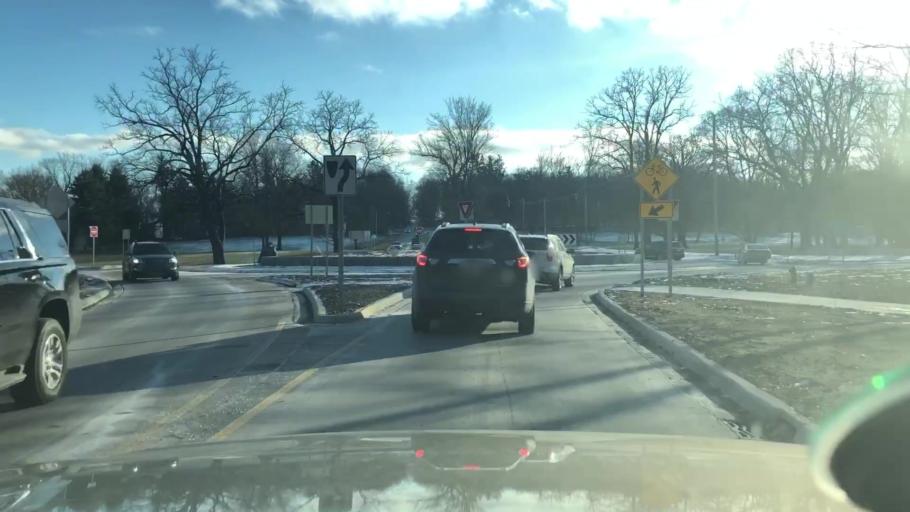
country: US
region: Michigan
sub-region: Jackson County
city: Jackson
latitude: 42.2177
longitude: -84.4183
